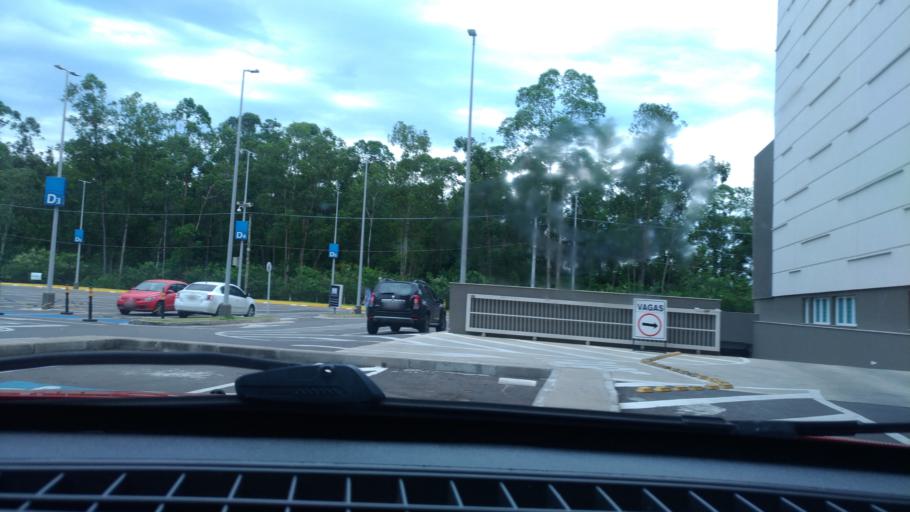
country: BR
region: Rio Grande do Sul
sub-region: Canoas
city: Canoas
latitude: -29.9143
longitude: -51.1643
